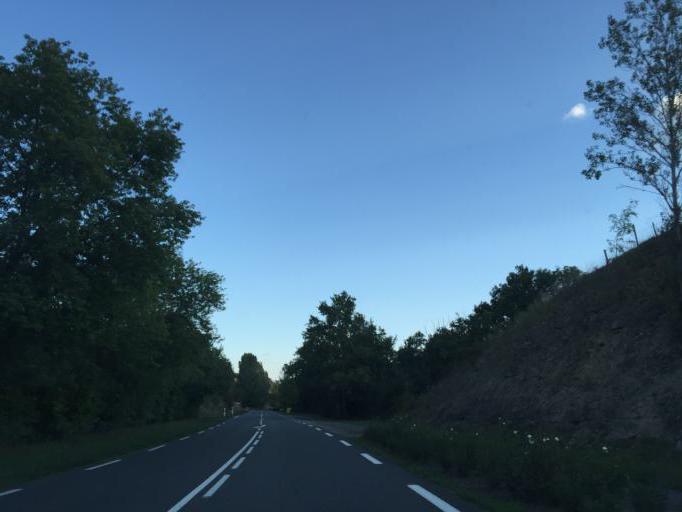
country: FR
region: Midi-Pyrenees
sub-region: Departement de l'Aveyron
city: Rodez
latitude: 44.3878
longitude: 2.5663
